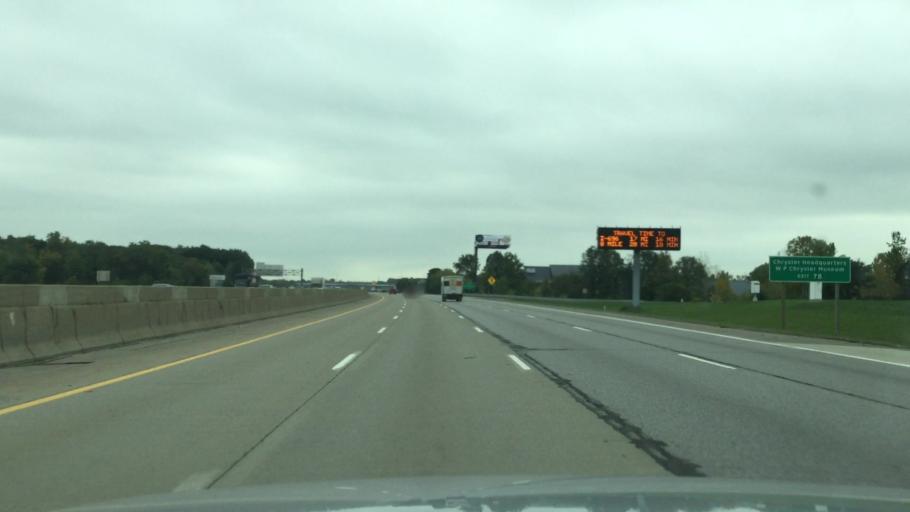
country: US
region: Michigan
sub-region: Oakland County
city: Auburn Hills
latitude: 42.6635
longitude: -83.2412
